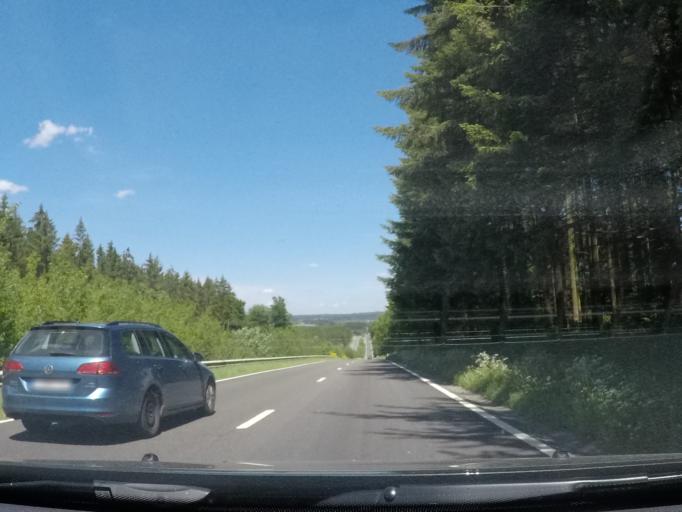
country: BE
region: Wallonia
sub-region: Province du Luxembourg
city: Saint-Hubert
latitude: 49.9533
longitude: 5.3548
